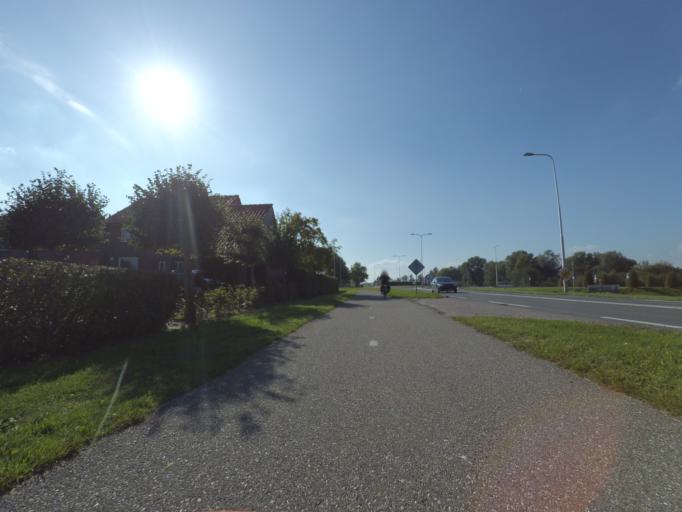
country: NL
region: Gelderland
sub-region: Gemeente Harderwijk
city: Harderwijk
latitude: 52.3704
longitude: 5.6137
